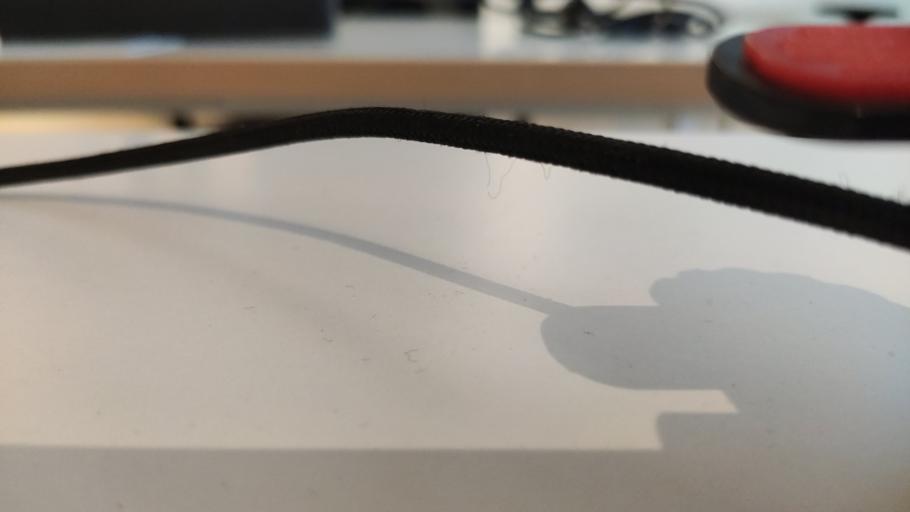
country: RU
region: Moskovskaya
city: Novopetrovskoye
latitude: 55.9029
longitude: 36.4387
